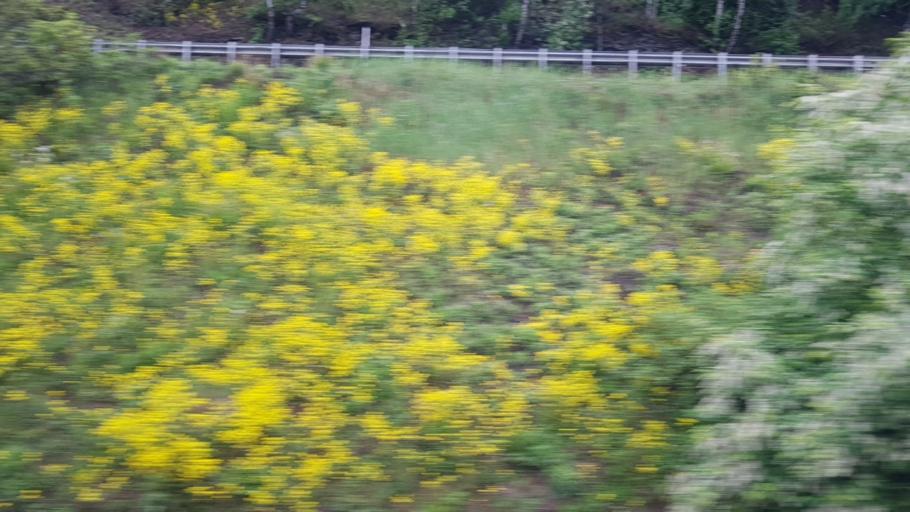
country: NO
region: Oppland
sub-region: Sor-Fron
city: Hundorp
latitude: 61.5466
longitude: 10.0281
